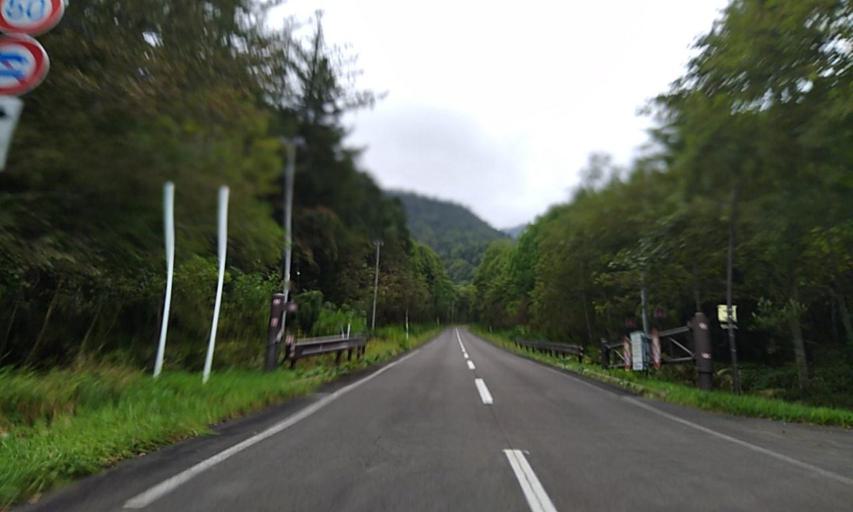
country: JP
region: Hokkaido
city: Bihoro
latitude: 43.5836
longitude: 144.2665
